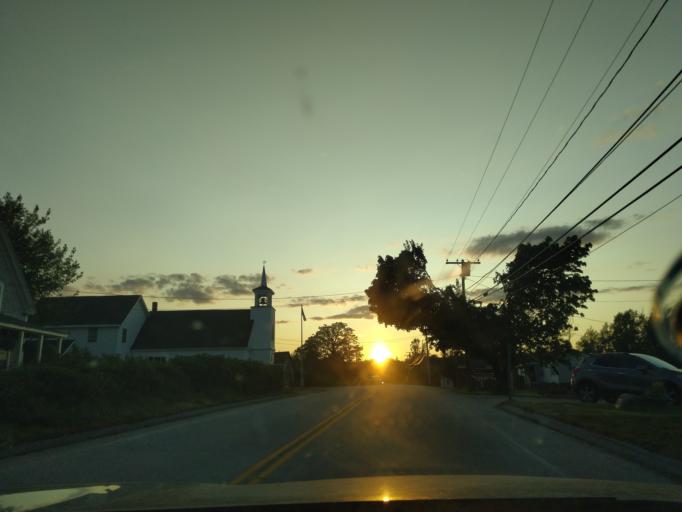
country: US
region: Maine
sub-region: Hancock County
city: Gouldsboro
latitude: 44.3896
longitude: -68.0404
